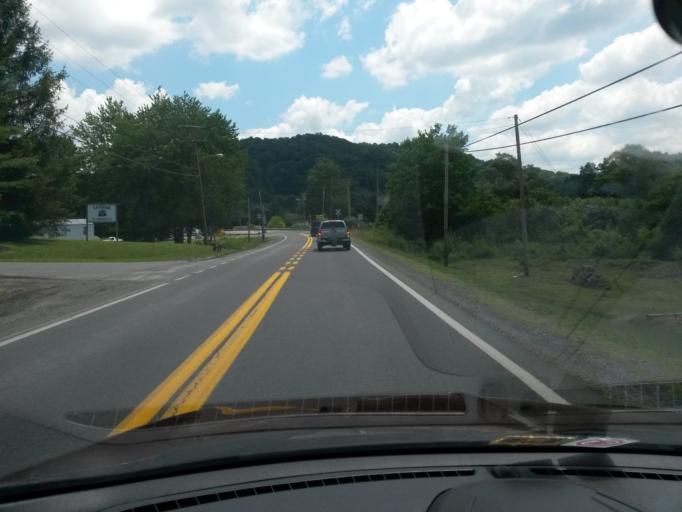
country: US
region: West Virginia
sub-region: Raleigh County
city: Sophia
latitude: 37.7290
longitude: -81.3057
